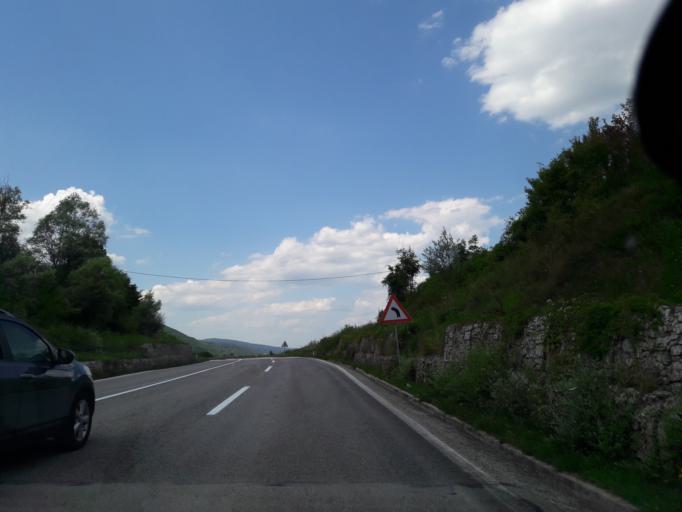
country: BA
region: Republika Srpska
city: Mrkonjic Grad
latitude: 44.4866
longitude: 17.1619
